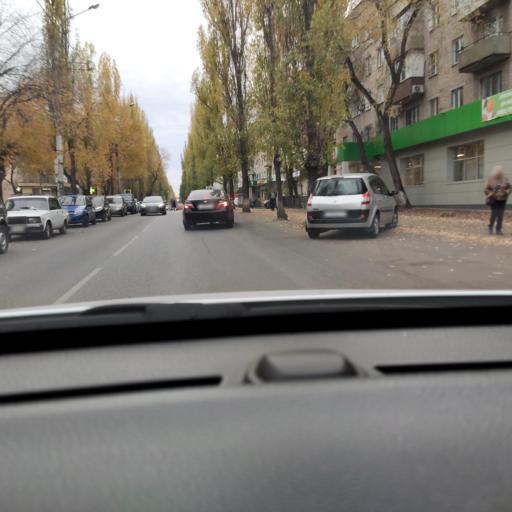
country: RU
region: Voronezj
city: Voronezh
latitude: 51.6895
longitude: 39.2601
